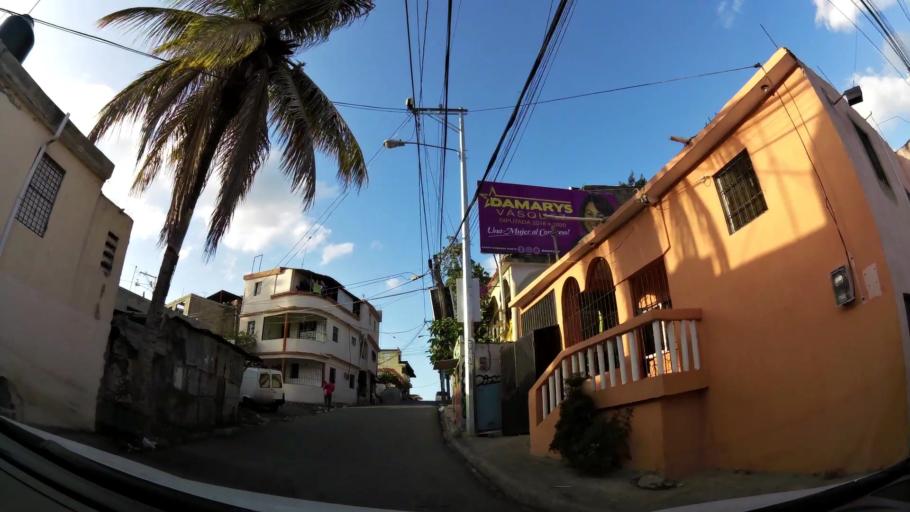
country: DO
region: Nacional
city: La Agustina
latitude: 18.5446
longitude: -69.9247
